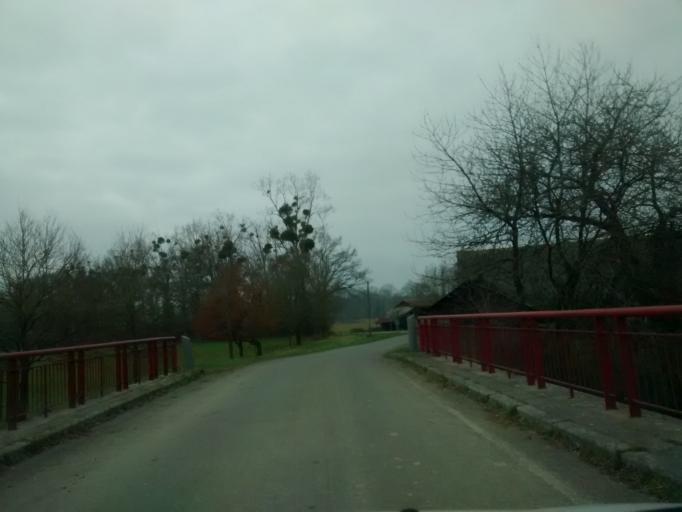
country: FR
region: Brittany
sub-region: Departement d'Ille-et-Vilaine
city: Sens-de-Bretagne
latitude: 48.3691
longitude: -1.5030
